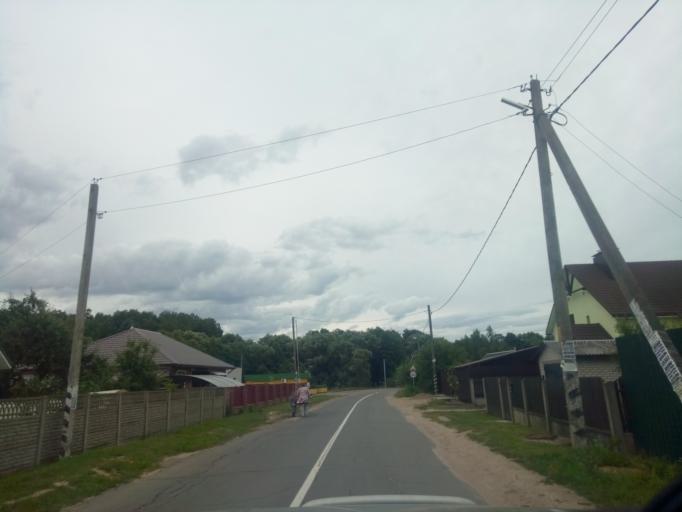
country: BY
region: Minsk
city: Zhdanovichy
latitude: 53.9296
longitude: 27.3824
